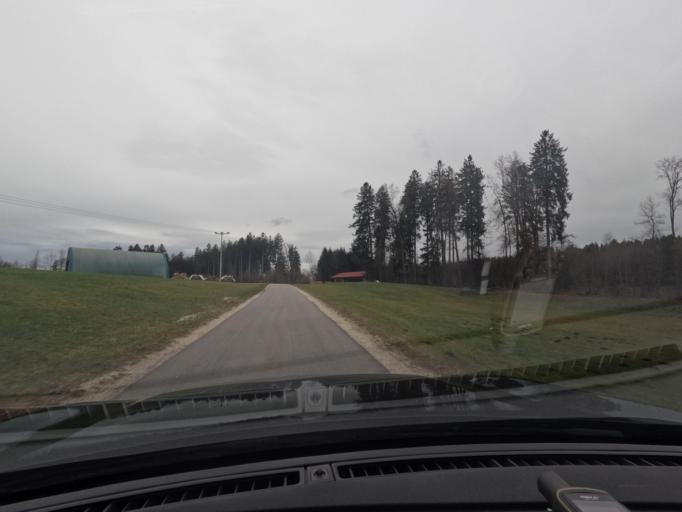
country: DE
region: Bavaria
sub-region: Upper Bavaria
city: Surberg
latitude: 47.8716
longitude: 12.6723
